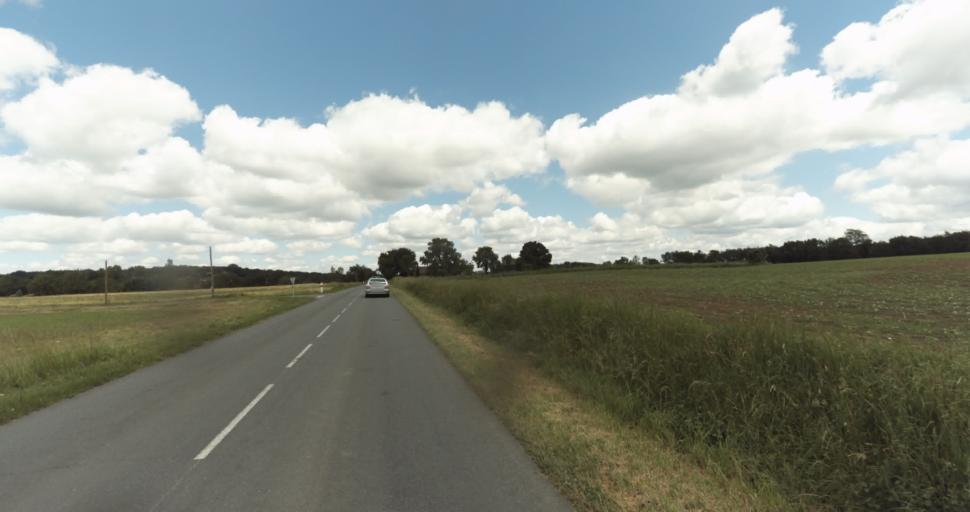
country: FR
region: Aquitaine
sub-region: Departement de la Dordogne
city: Beaumont-du-Perigord
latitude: 44.7147
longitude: 0.7507
